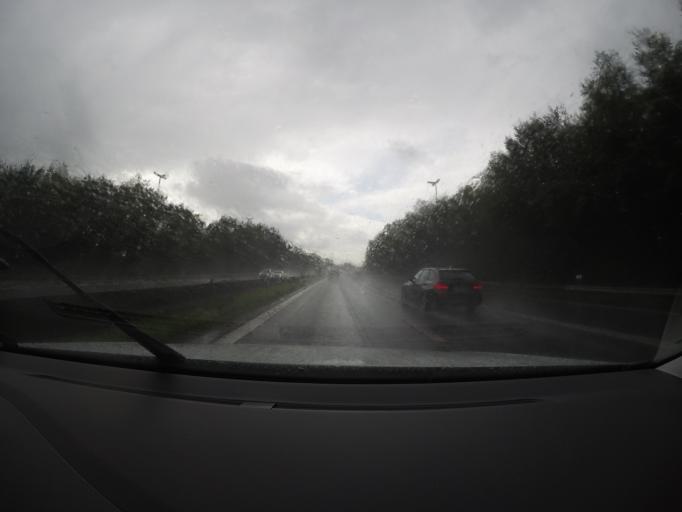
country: BE
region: Wallonia
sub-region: Province du Brabant Wallon
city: Braine-l'Alleud
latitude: 50.6613
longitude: 4.3766
